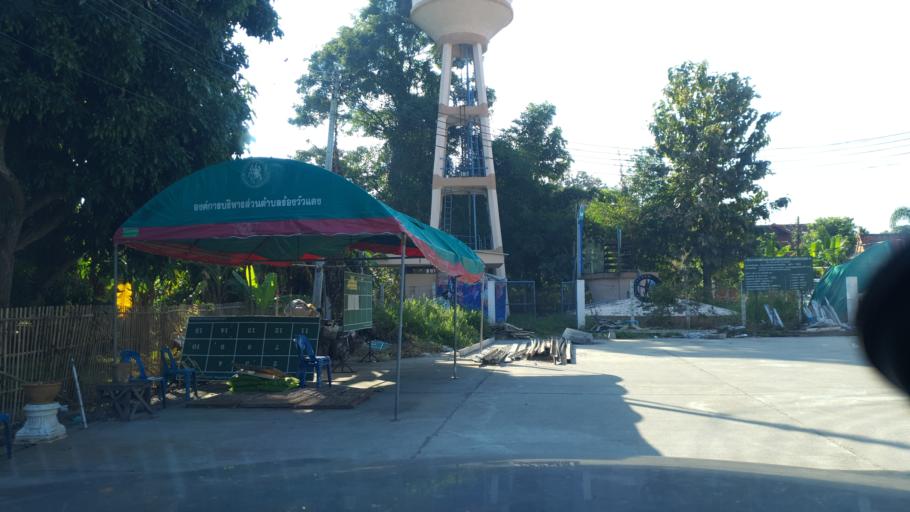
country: TH
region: Chiang Mai
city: Mae On
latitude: 18.7415
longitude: 99.1935
